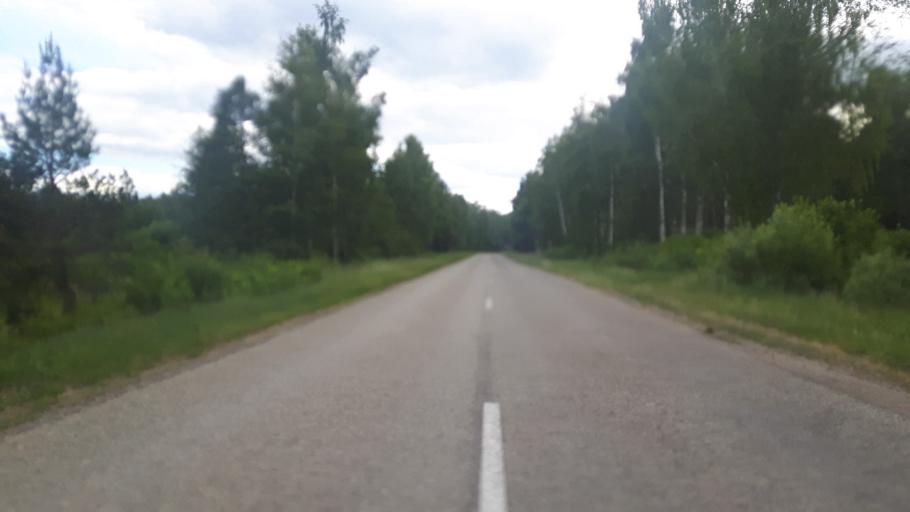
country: LV
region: Engure
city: Smarde
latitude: 57.0295
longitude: 23.3601
